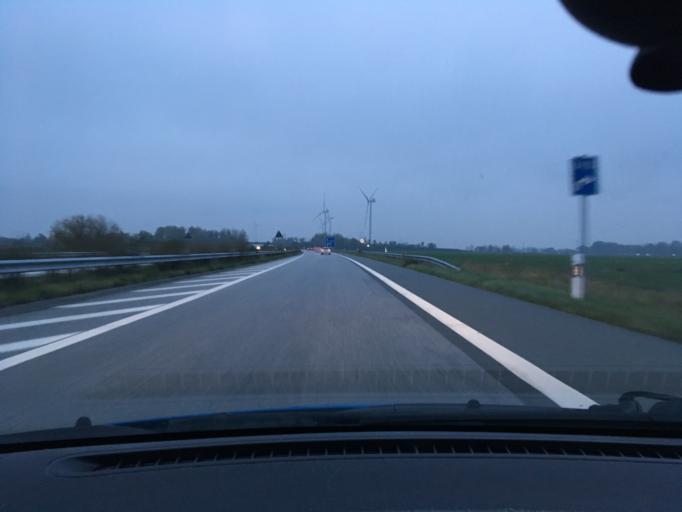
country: DE
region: Schleswig-Holstein
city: Lohe-Rickelshof
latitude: 54.1961
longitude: 9.0449
